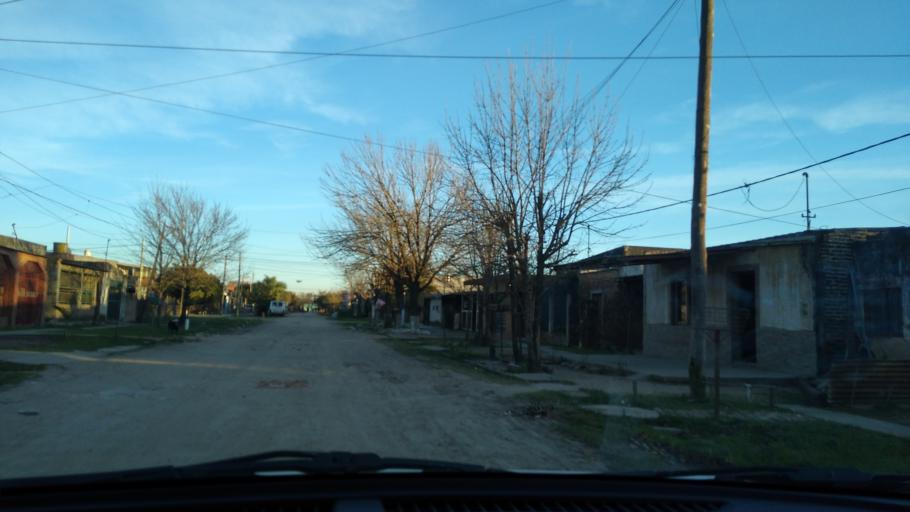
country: AR
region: Chaco
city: Resistencia
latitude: -27.4768
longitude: -58.9678
